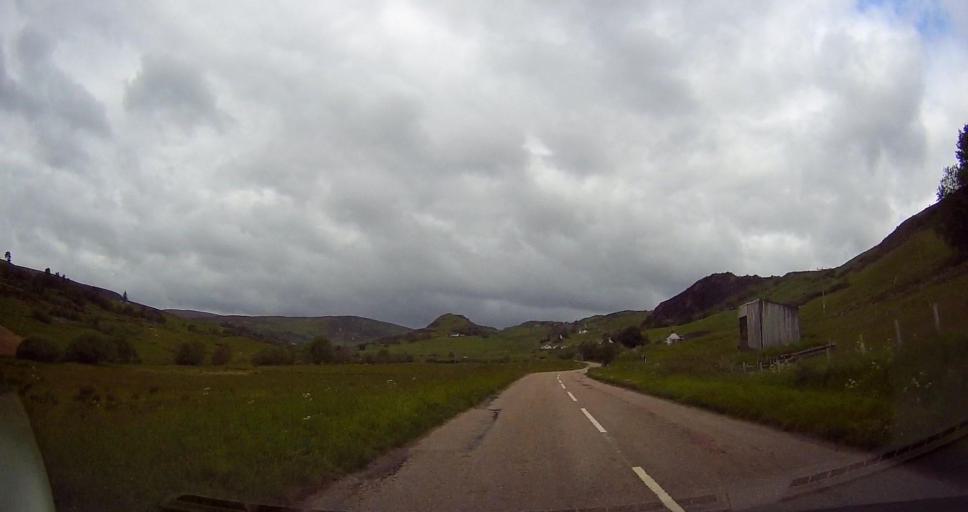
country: GB
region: Scotland
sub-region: Highland
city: Dornoch
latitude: 58.0053
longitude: -4.2334
